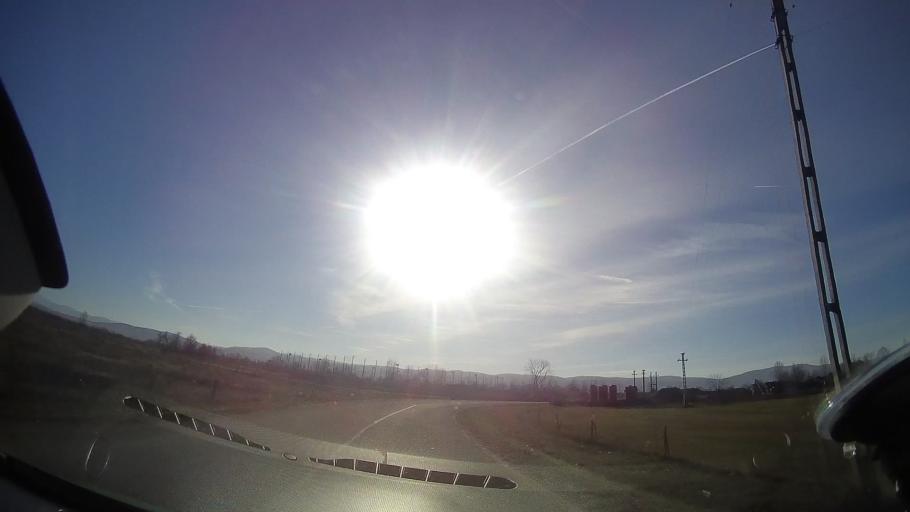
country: RO
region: Bihor
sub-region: Comuna Auseu
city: Auseu
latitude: 47.0296
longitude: 22.4928
